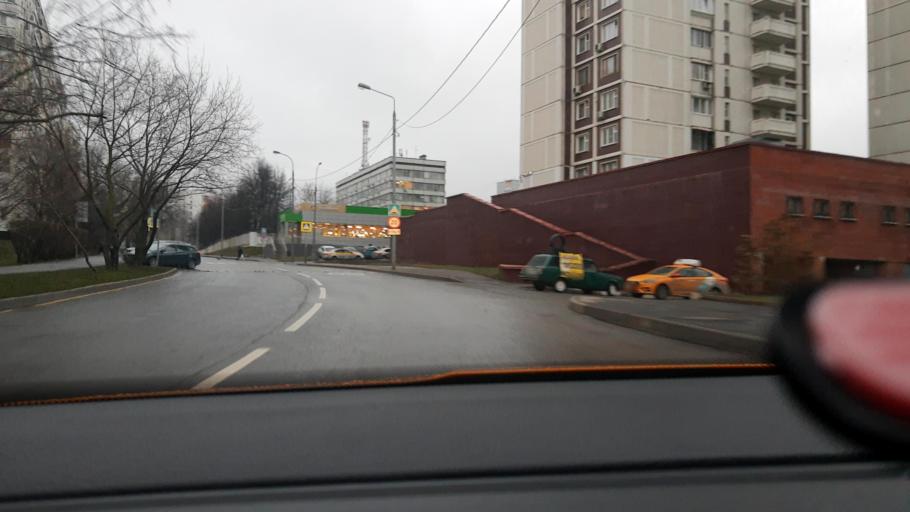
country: RU
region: Moscow
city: Strogino
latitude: 55.8575
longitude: 37.4065
